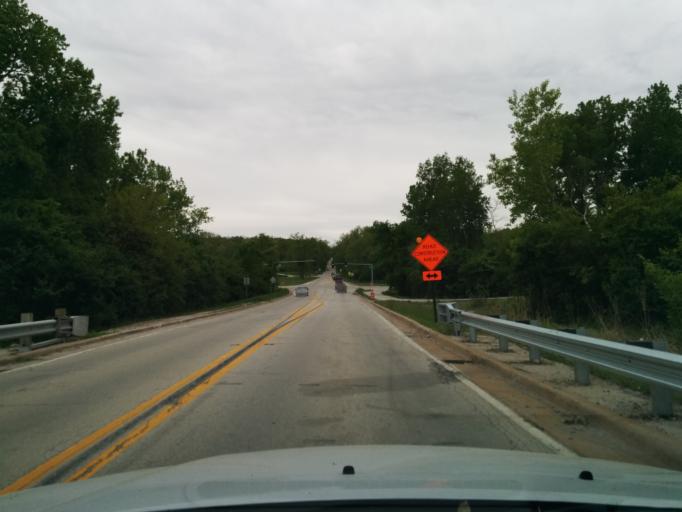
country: US
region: Illinois
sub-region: Cook County
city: Palos Park
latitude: 41.6871
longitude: -87.8749
